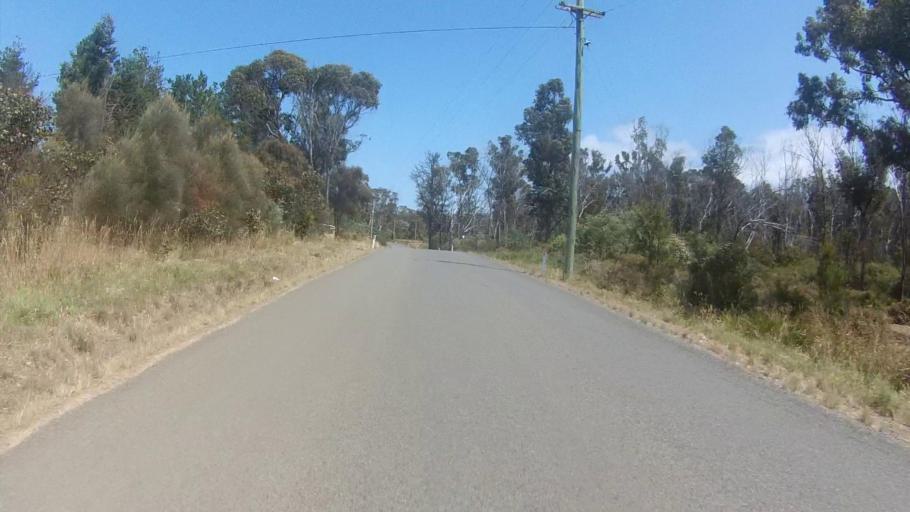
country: AU
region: Tasmania
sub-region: Sorell
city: Sorell
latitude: -42.8554
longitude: 147.8380
